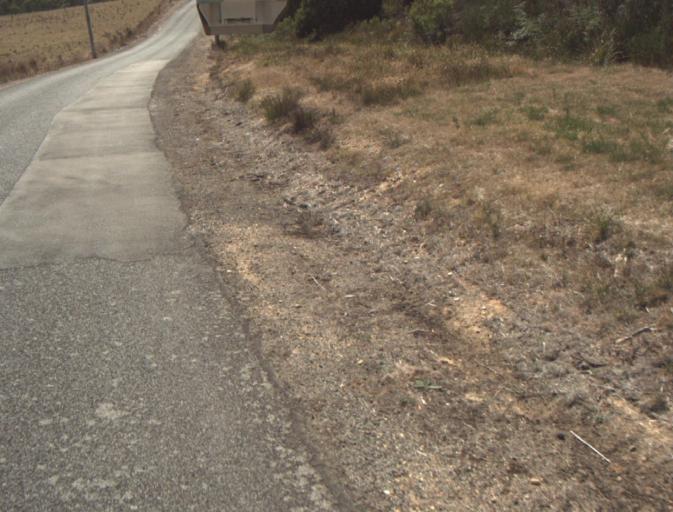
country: AU
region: Tasmania
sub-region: Launceston
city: Newstead
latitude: -41.3199
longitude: 147.3240
